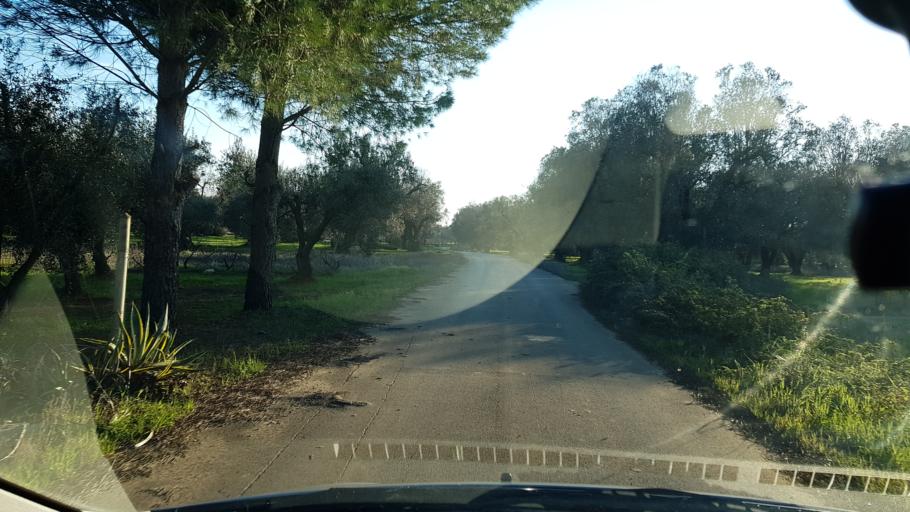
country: IT
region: Apulia
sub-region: Provincia di Brindisi
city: Mesagne
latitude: 40.5619
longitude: 17.8669
